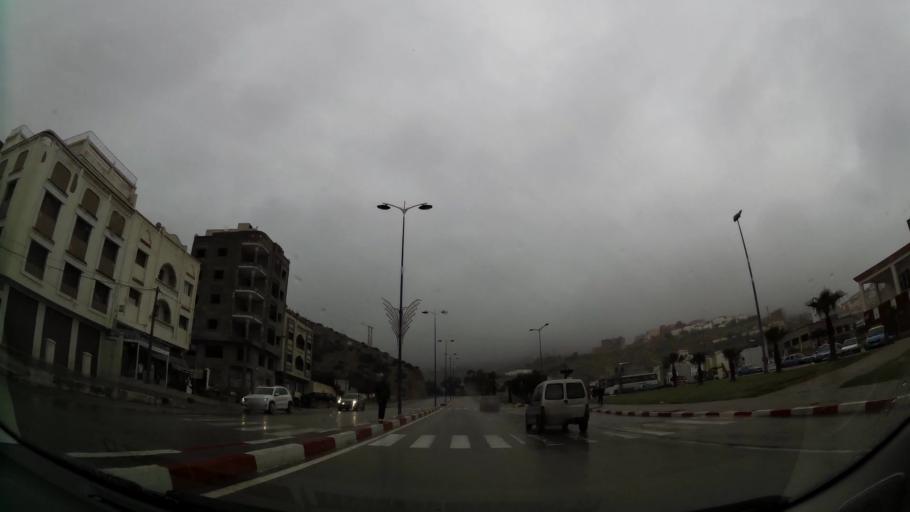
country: MA
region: Taza-Al Hoceima-Taounate
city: Al Hoceima
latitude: 35.2331
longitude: -3.9286
